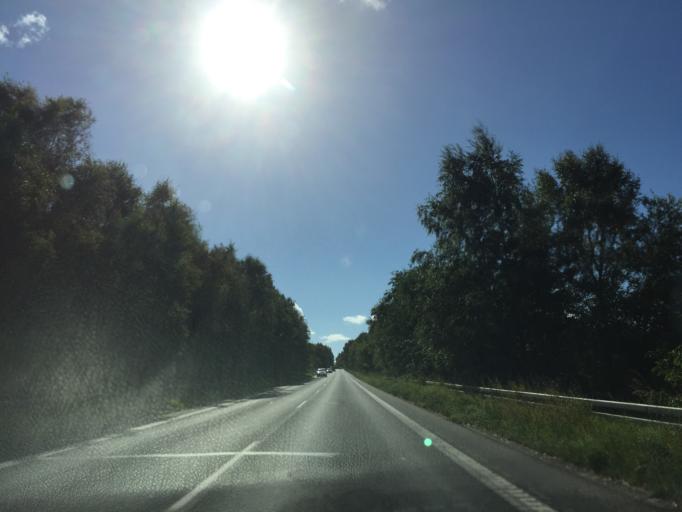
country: DK
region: Central Jutland
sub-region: Viborg Kommune
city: Bjerringbro
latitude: 56.3652
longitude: 9.6760
